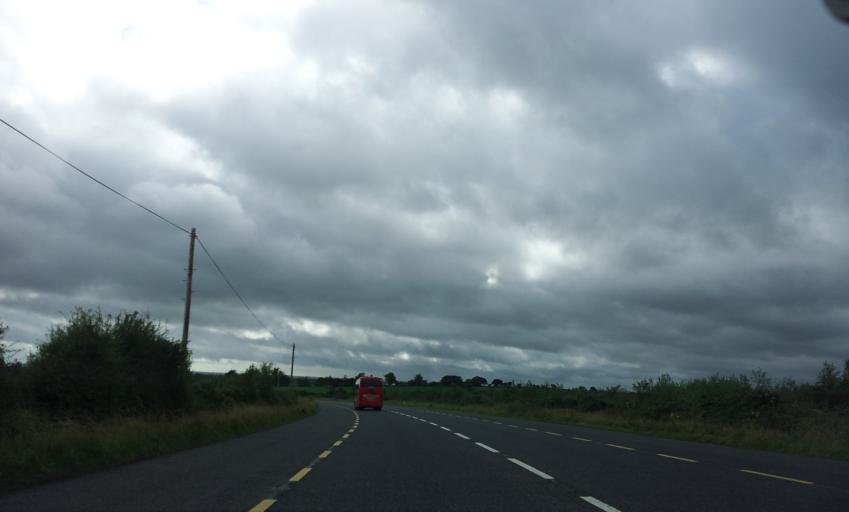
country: IE
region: Munster
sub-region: Waterford
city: Dungarvan
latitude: 52.0028
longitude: -7.7193
